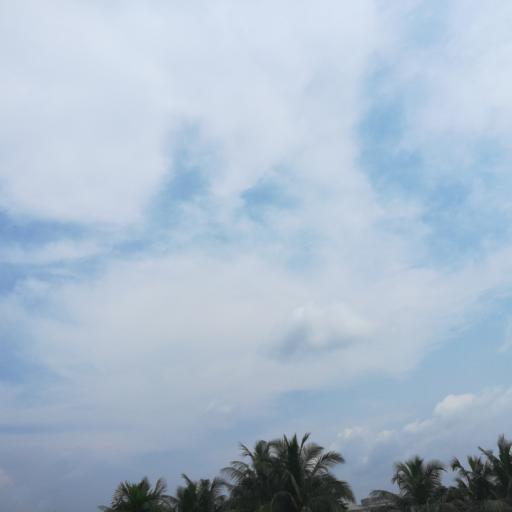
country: NG
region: Rivers
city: Port Harcourt
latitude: 4.8354
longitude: 7.0142
